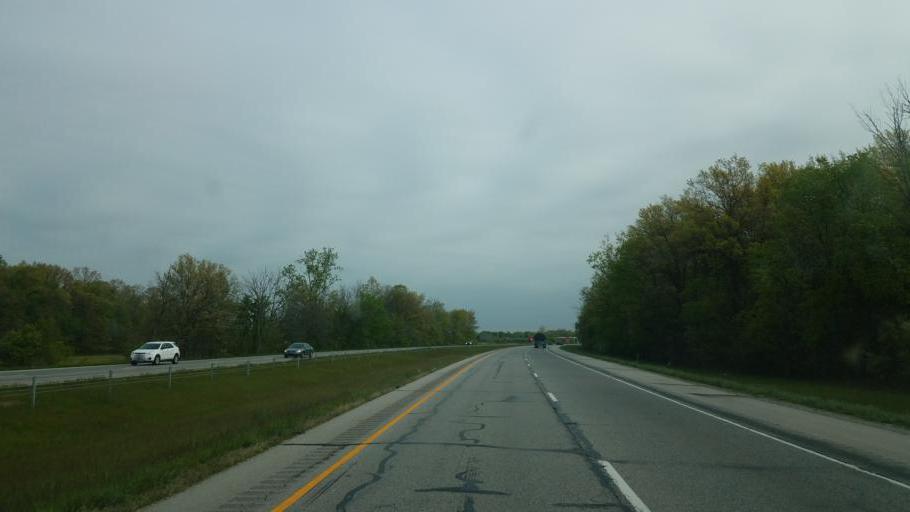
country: US
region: Indiana
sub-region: Allen County
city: Huntertown
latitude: 41.2149
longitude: -85.1047
